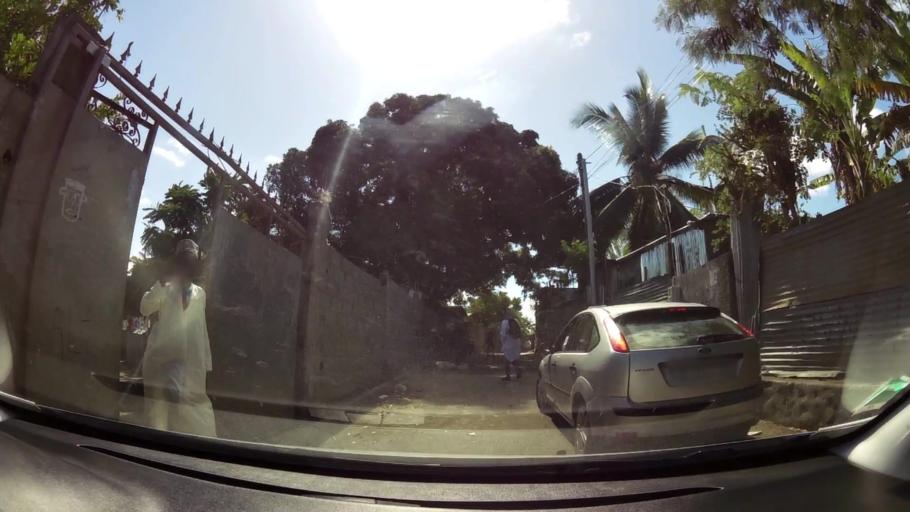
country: YT
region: Pamandzi
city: Pamandzi
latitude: -12.7893
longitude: 45.2822
